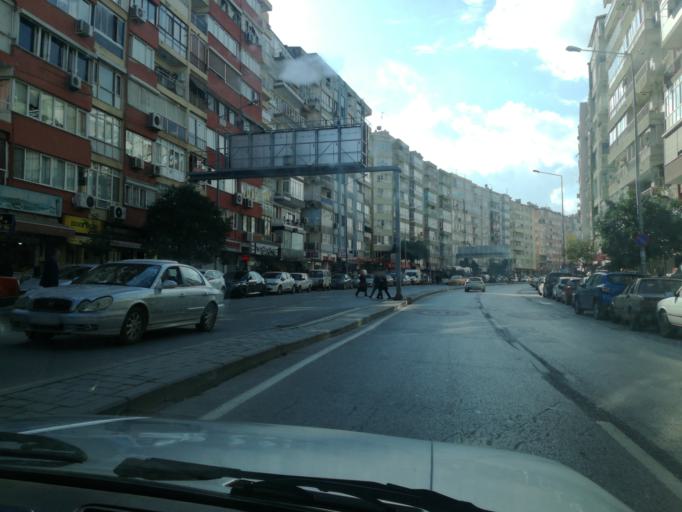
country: TR
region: Izmir
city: Izmir
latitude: 38.4095
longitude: 27.1273
